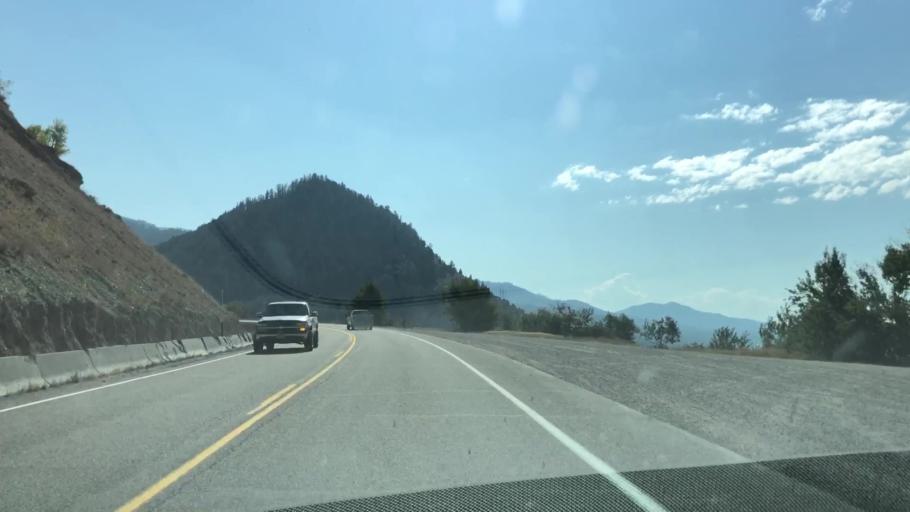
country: US
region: Idaho
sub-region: Teton County
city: Victor
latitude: 43.3194
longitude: -111.1554
